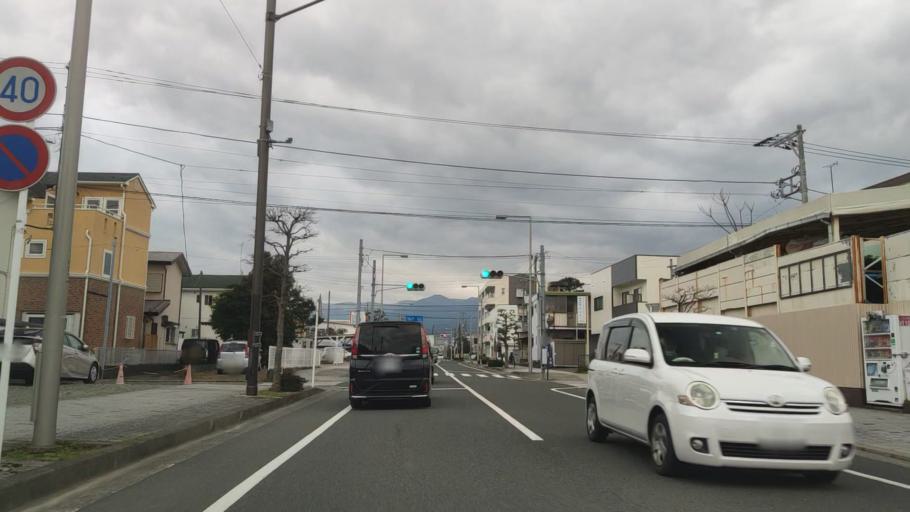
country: JP
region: Kanagawa
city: Odawara
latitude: 35.2656
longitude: 139.1718
